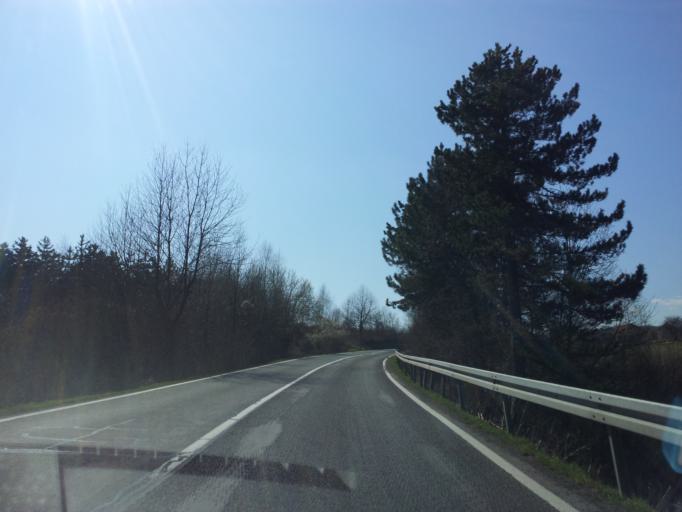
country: HR
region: Licko-Senjska
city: Jezerce
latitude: 44.9862
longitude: 15.6475
